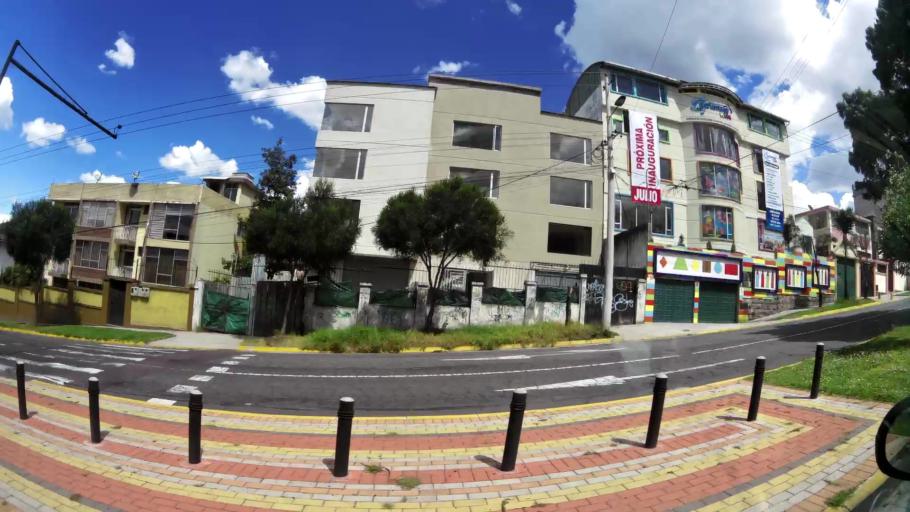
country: EC
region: Pichincha
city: Quito
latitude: -0.2053
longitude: -78.5079
